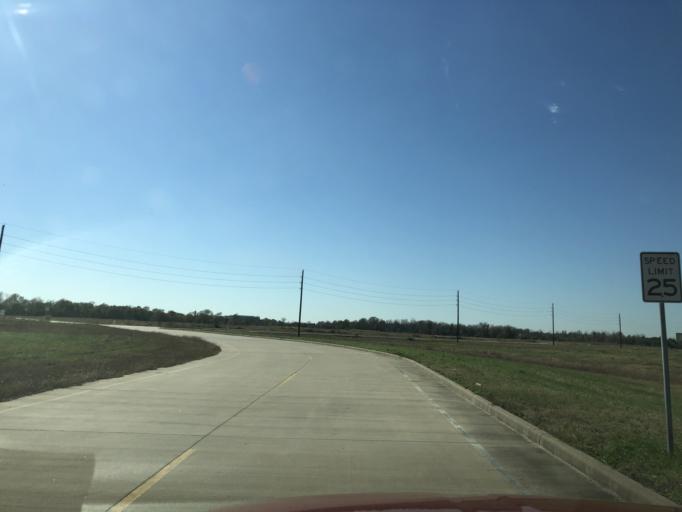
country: US
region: Texas
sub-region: Brazoria County
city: Brookside Village
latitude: 29.5896
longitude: -95.3880
